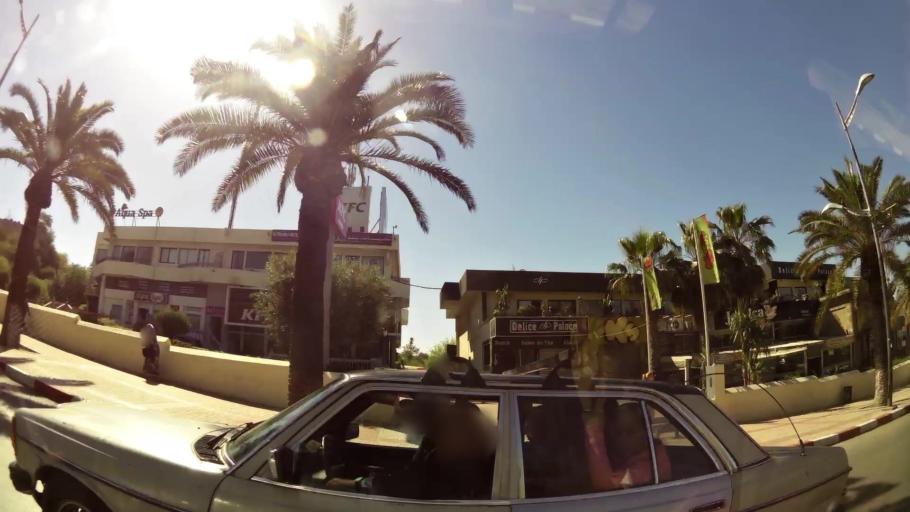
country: MA
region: Meknes-Tafilalet
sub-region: Meknes
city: Meknes
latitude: 33.8970
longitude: -5.5545
